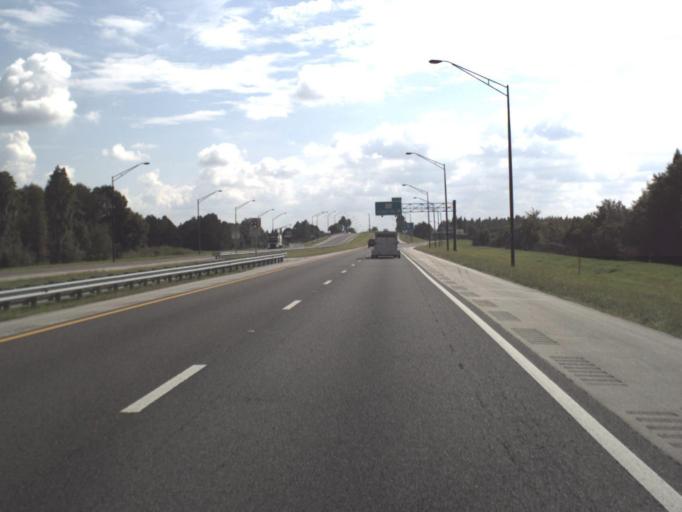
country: US
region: Florida
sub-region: Polk County
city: Winston
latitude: 28.0105
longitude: -82.0236
